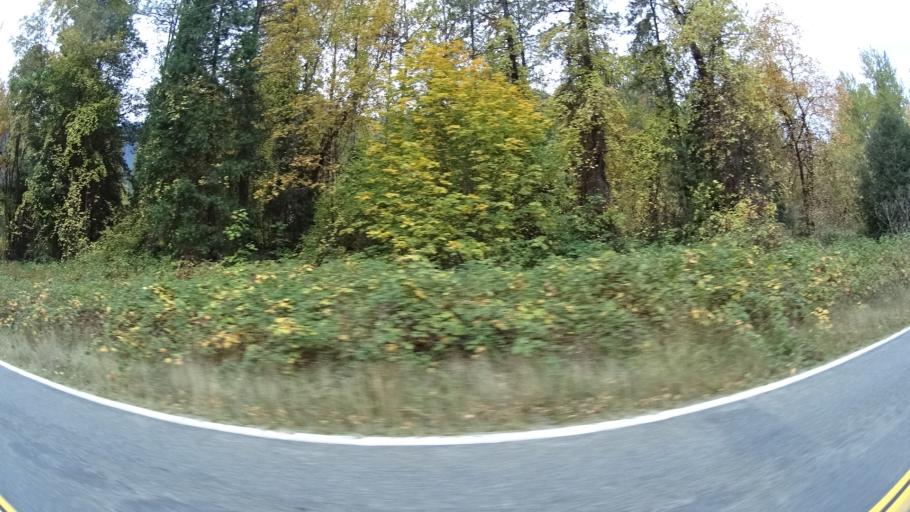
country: US
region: California
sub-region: Siskiyou County
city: Happy Camp
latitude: 41.8653
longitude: -123.4028
